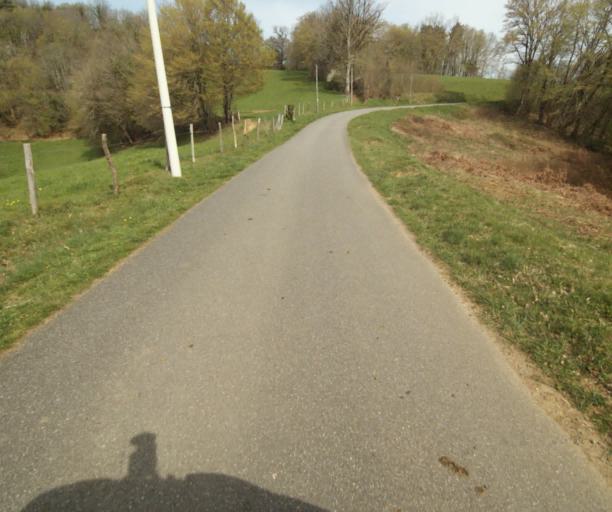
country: FR
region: Limousin
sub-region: Departement de la Correze
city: Naves
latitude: 45.3308
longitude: 1.8026
